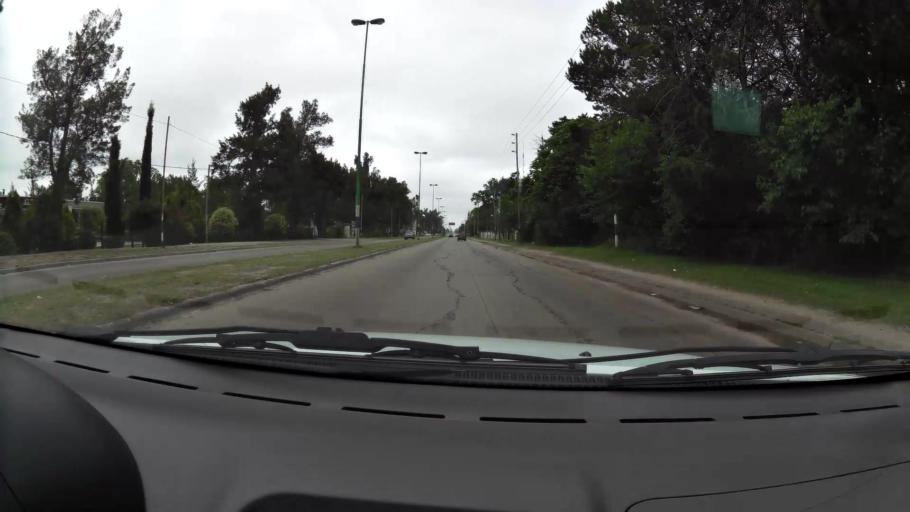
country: AR
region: Buenos Aires
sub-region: Partido de La Plata
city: La Plata
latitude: -34.9585
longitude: -58.0077
